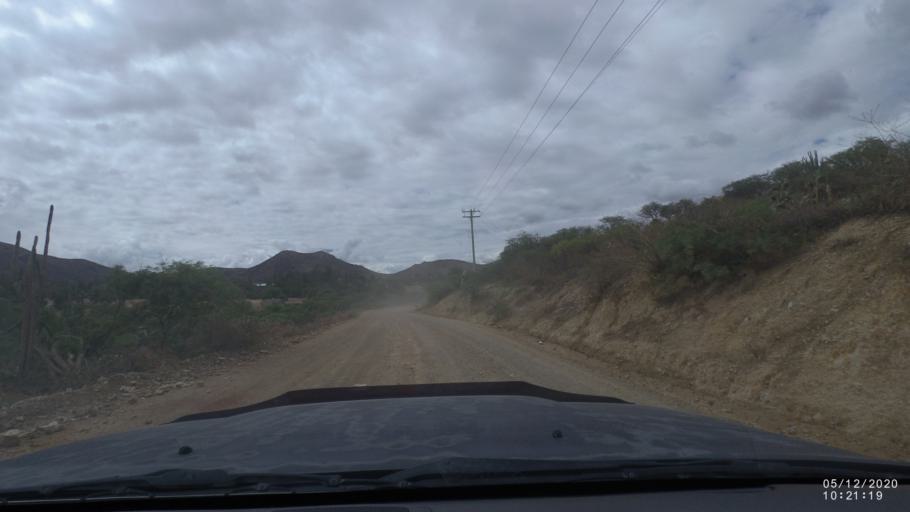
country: BO
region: Cochabamba
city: Sipe Sipe
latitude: -17.4890
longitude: -66.2821
